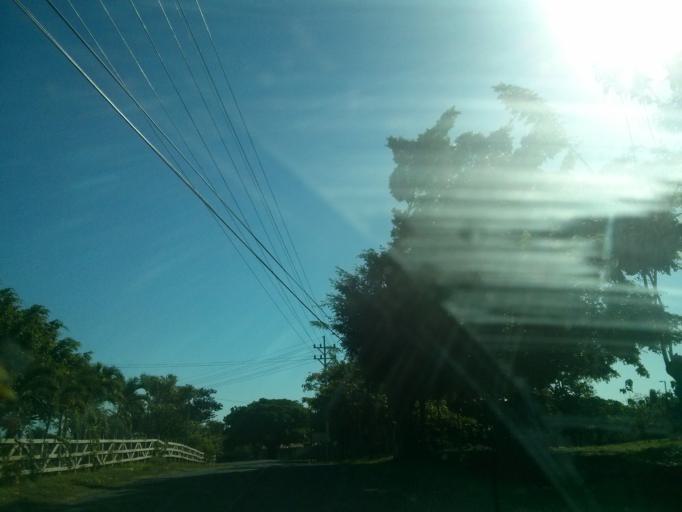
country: CR
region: Puntarenas
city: Paquera
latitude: 9.6936
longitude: -85.0976
